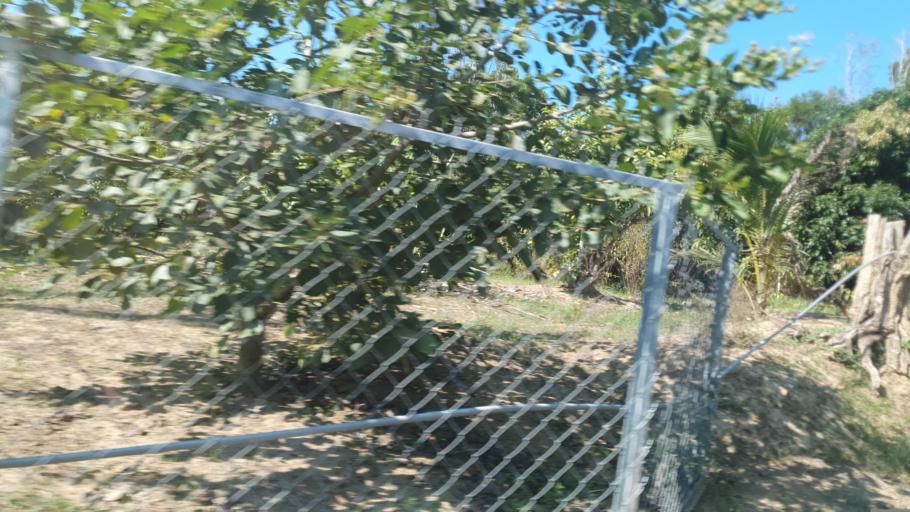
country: TW
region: Taiwan
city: Yujing
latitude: 23.0442
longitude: 120.3647
